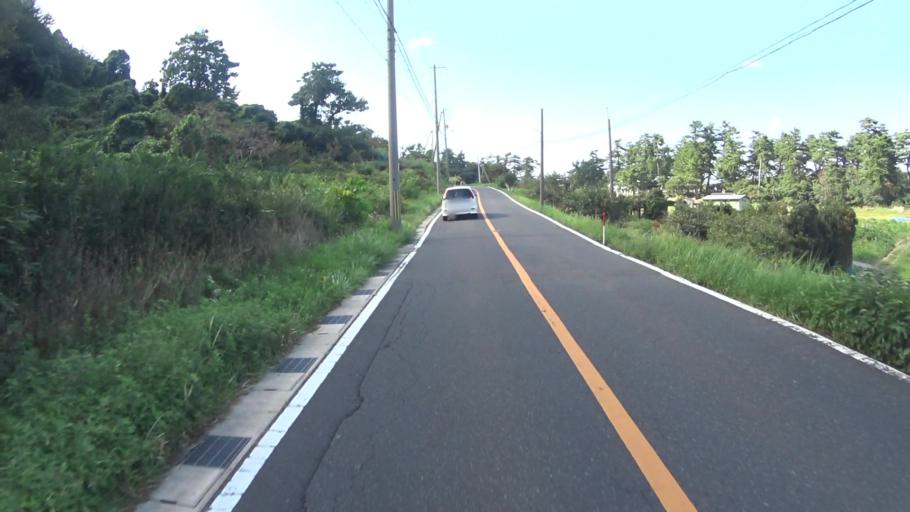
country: JP
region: Kyoto
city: Miyazu
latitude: 35.7499
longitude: 135.1600
